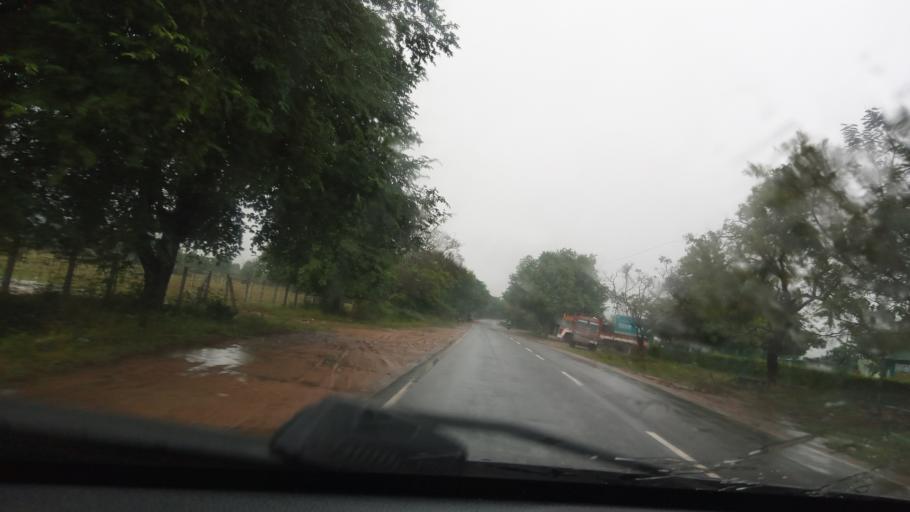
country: IN
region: Tamil Nadu
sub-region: Vellore
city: Kalavai
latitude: 12.8288
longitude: 79.4063
